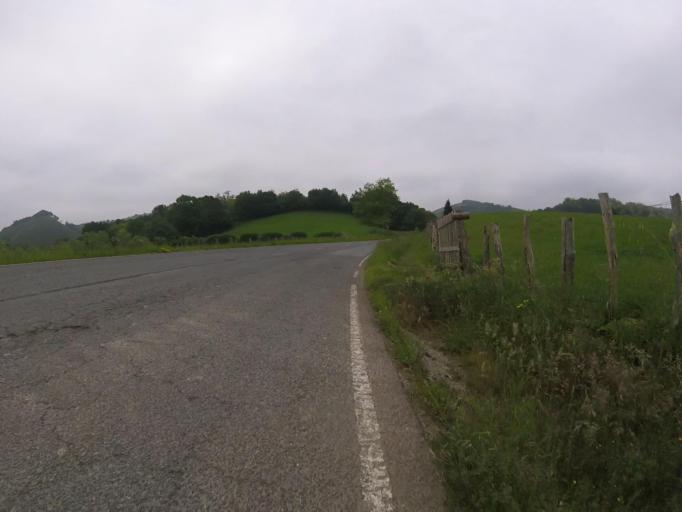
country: ES
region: Navarre
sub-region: Provincia de Navarra
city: Zugarramurdi
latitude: 43.2747
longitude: -1.4968
